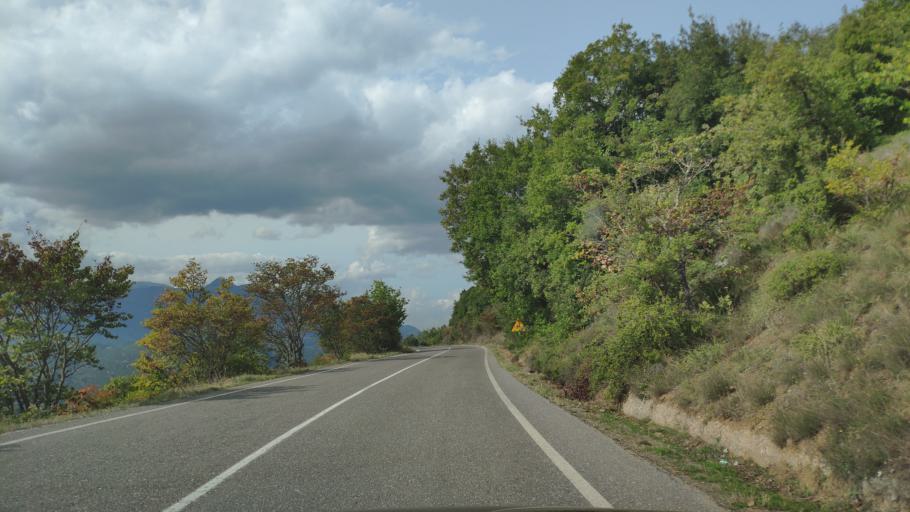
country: GR
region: Central Greece
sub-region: Nomos Fthiotidos
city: Anthili
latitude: 38.7394
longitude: 22.4475
